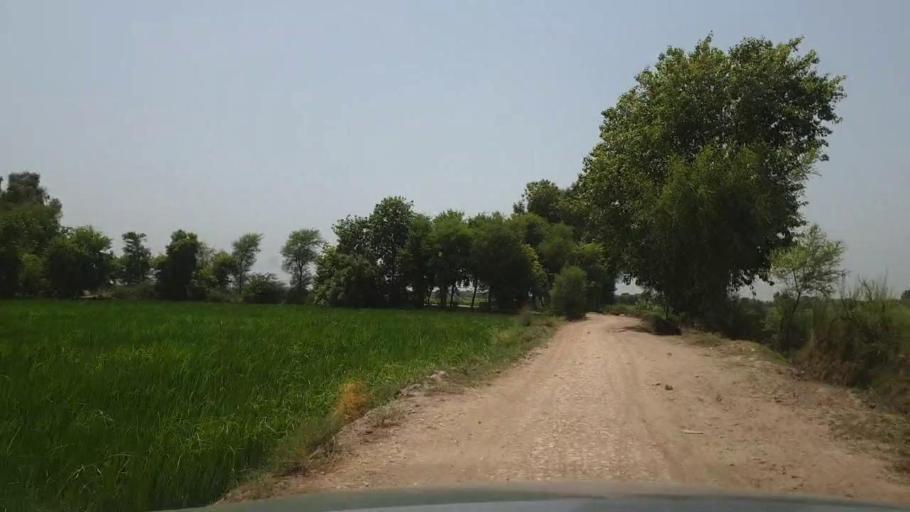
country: PK
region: Sindh
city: Ratodero
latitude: 27.7897
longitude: 68.3477
